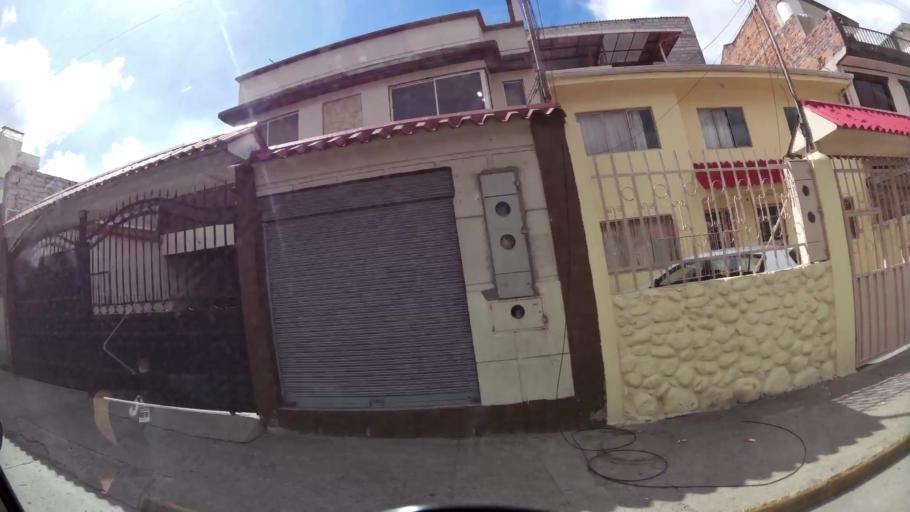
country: EC
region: Azuay
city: Cuenca
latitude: -2.8864
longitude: -78.9925
